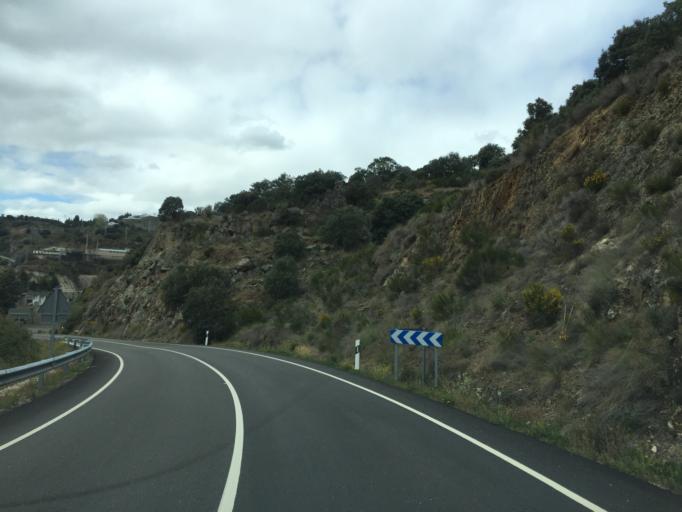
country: PT
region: Braganca
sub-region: Miranda do Douro
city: Miranda do Douro
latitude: 41.4890
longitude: -6.2592
